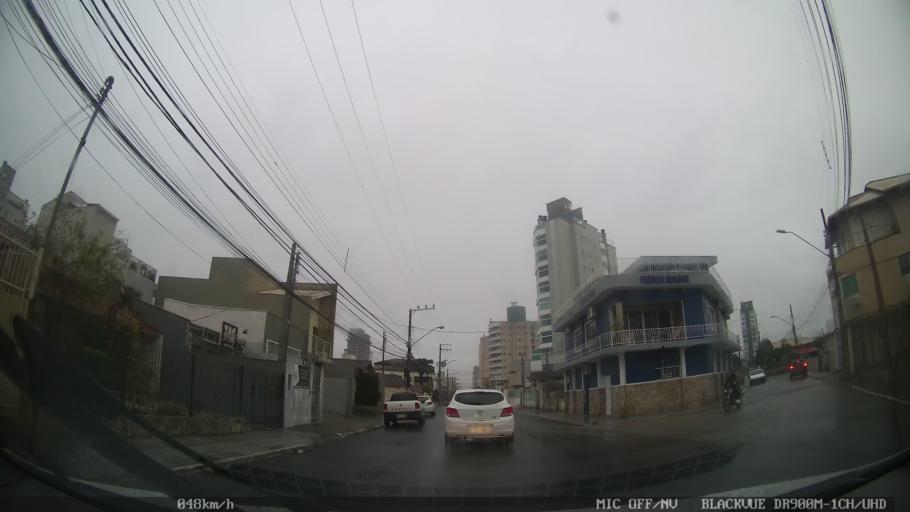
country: BR
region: Santa Catarina
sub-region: Itajai
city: Itajai
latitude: -26.9123
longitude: -48.6701
